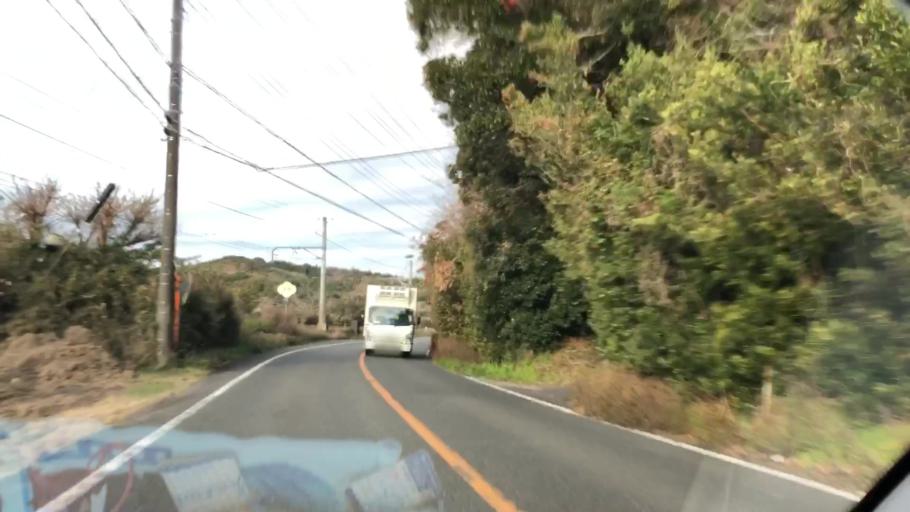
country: JP
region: Chiba
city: Tateyama
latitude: 34.9904
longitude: 139.9253
